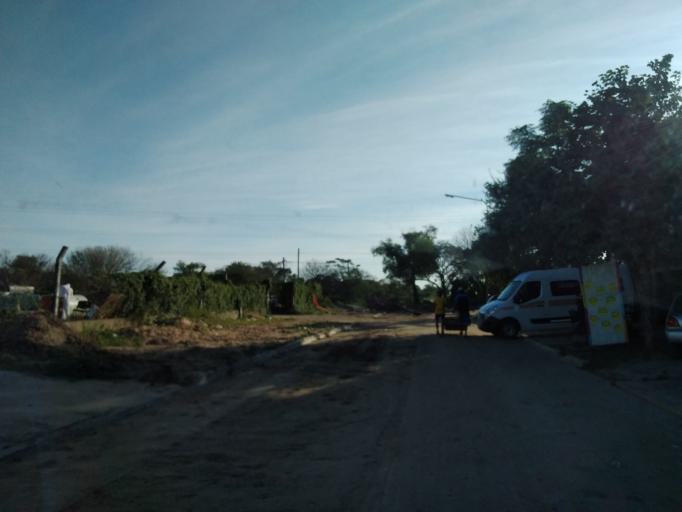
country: AR
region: Corrientes
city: Corrientes
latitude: -27.5042
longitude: -58.8355
